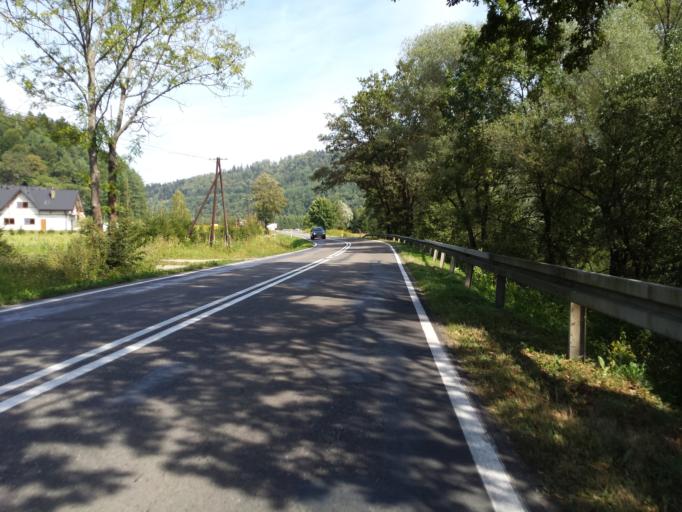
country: PL
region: Subcarpathian Voivodeship
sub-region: Powiat leski
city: Lesko
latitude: 49.4393
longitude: 22.3461
